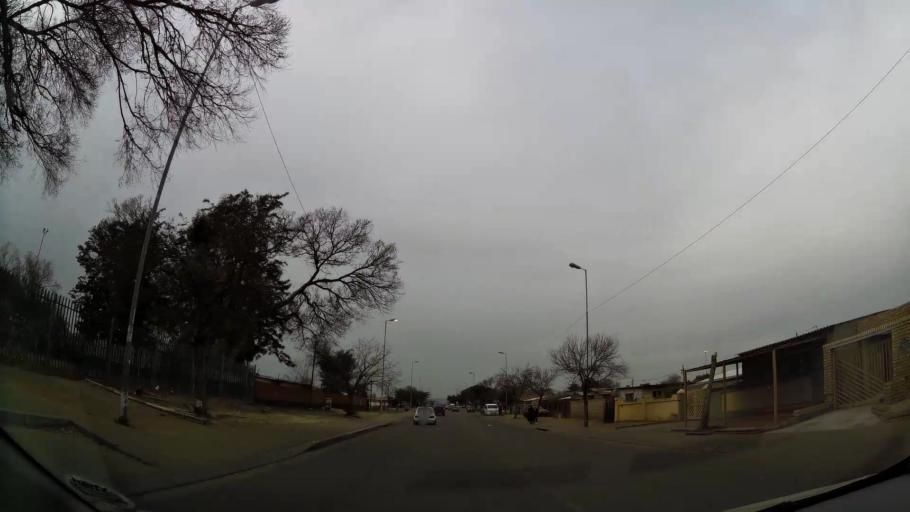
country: ZA
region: Gauteng
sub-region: City of Tshwane Metropolitan Municipality
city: Pretoria
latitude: -25.7110
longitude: 28.3444
